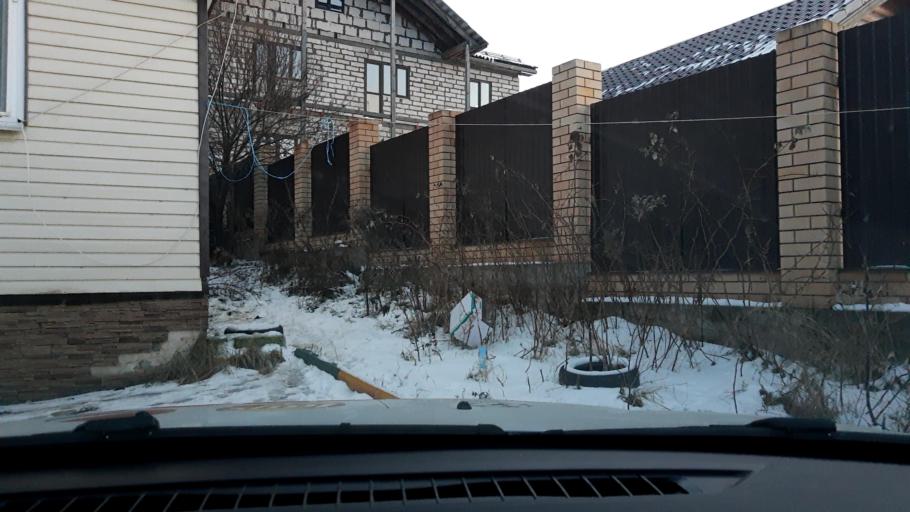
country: RU
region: Nizjnij Novgorod
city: Burevestnik
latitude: 56.1979
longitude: 43.8915
